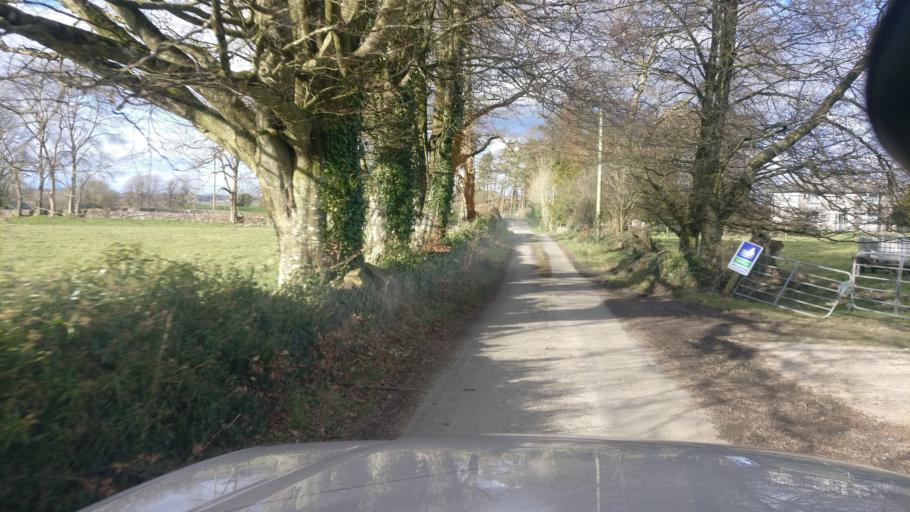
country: IE
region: Connaught
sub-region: County Galway
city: Loughrea
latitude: 53.1799
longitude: -8.4258
